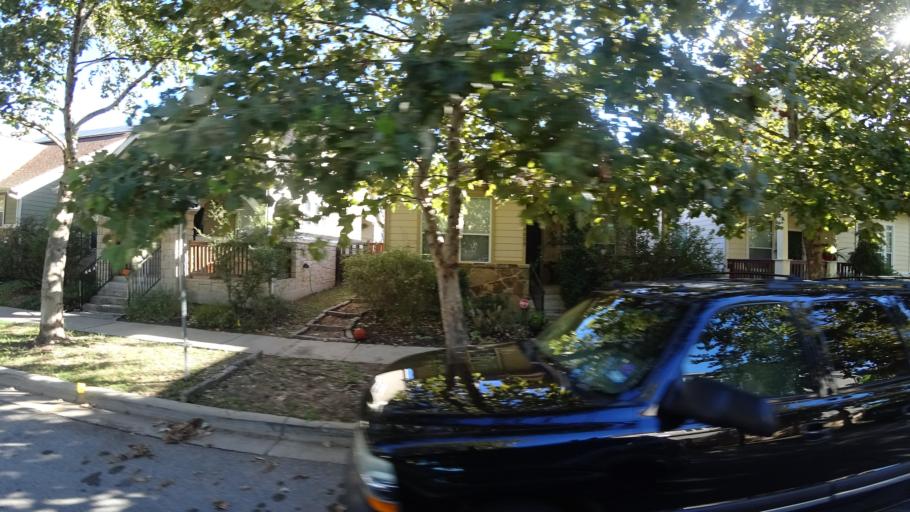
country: US
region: Texas
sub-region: Travis County
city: Austin
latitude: 30.2920
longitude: -97.7004
